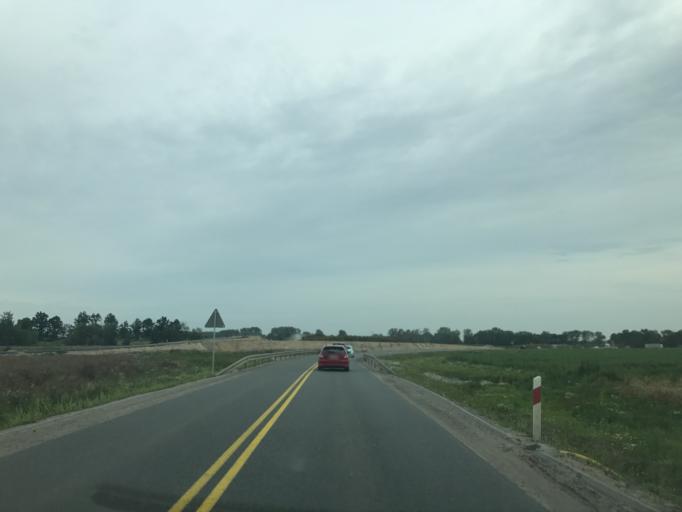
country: PL
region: Pomeranian Voivodeship
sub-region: Powiat gdanski
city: Cedry Wielkie
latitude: 54.2691
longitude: 18.8753
